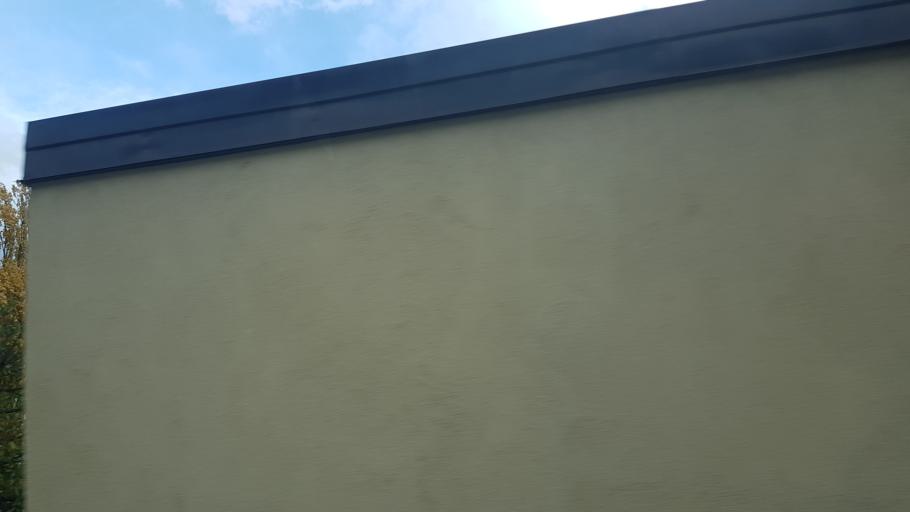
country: IT
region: Abruzzo
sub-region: Provincia dell' Aquila
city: Progetto Case Bazzano
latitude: 42.3600
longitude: 13.4300
